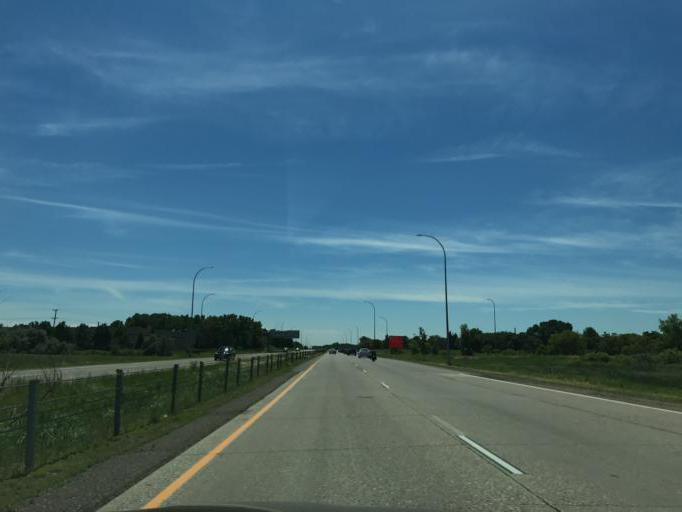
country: US
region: Minnesota
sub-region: Hennepin County
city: Osseo
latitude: 45.0940
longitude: -93.4025
